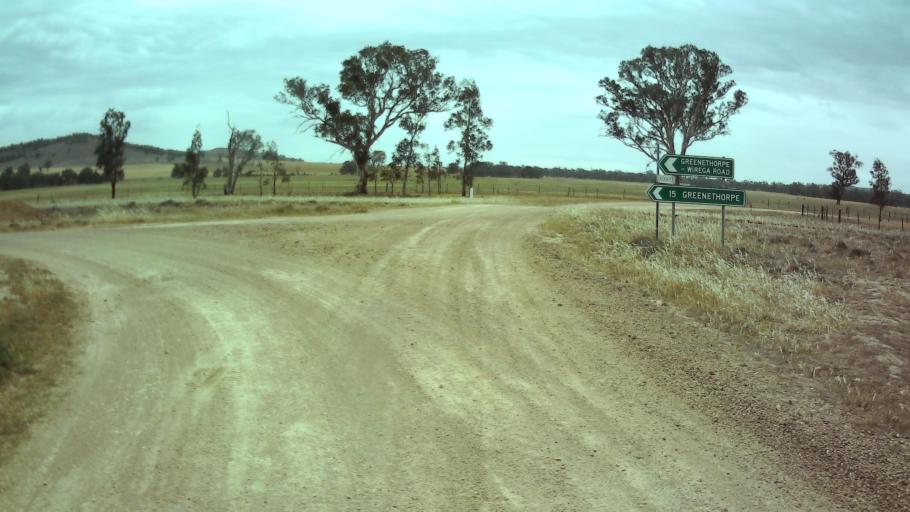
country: AU
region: New South Wales
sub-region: Weddin
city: Grenfell
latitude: -33.9324
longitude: 148.2786
